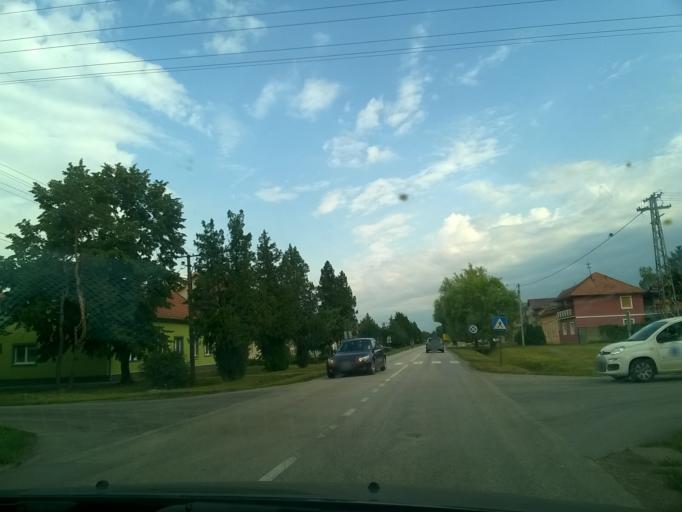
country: RS
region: Autonomna Pokrajina Vojvodina
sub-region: Juznobanatski Okrug
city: Kovacica
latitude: 45.1136
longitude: 20.6181
